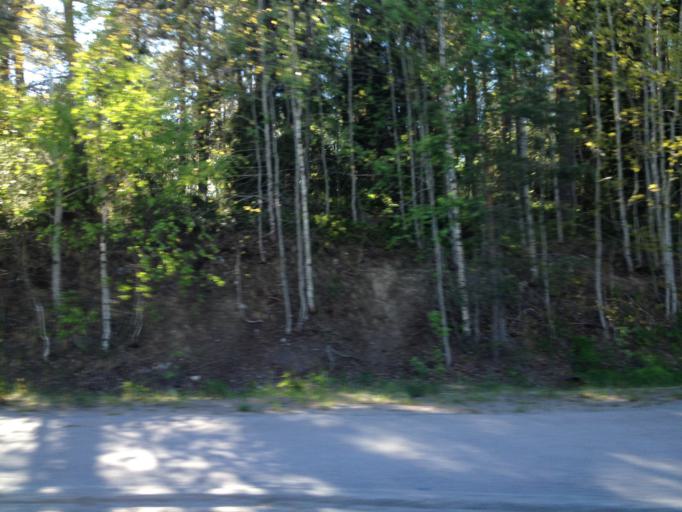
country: FI
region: Uusimaa
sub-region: Helsinki
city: Espoo
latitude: 60.2388
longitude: 24.5968
